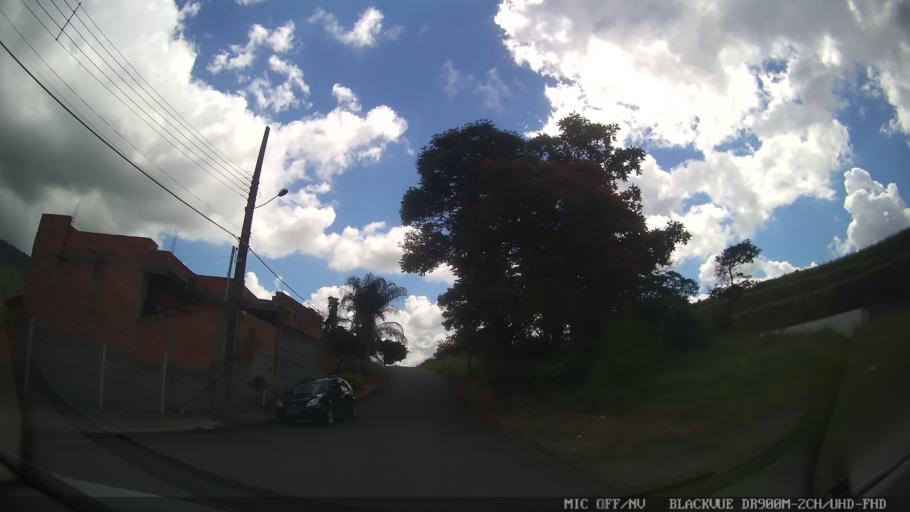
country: BR
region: Minas Gerais
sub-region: Extrema
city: Extrema
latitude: -22.8881
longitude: -46.4099
